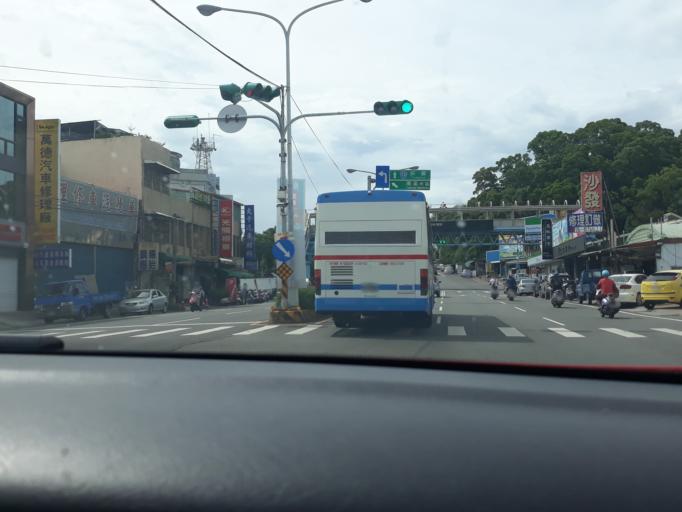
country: TW
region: Taiwan
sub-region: Miaoli
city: Miaoli
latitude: 24.5520
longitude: 120.8140
